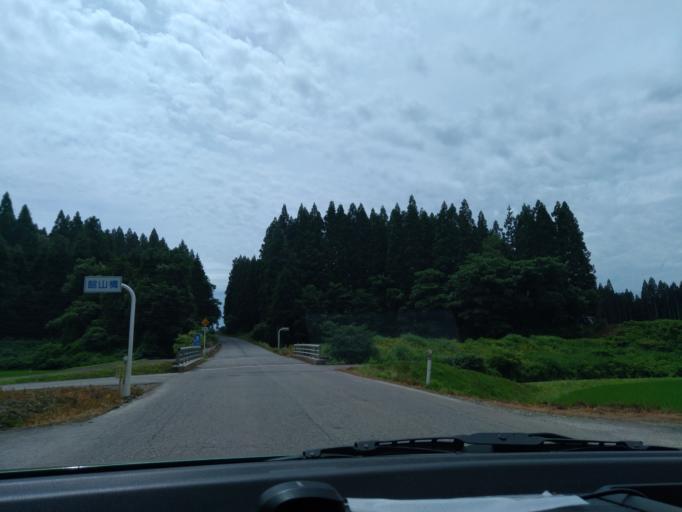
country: JP
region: Akita
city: Kakunodatemachi
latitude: 39.5896
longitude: 140.6196
